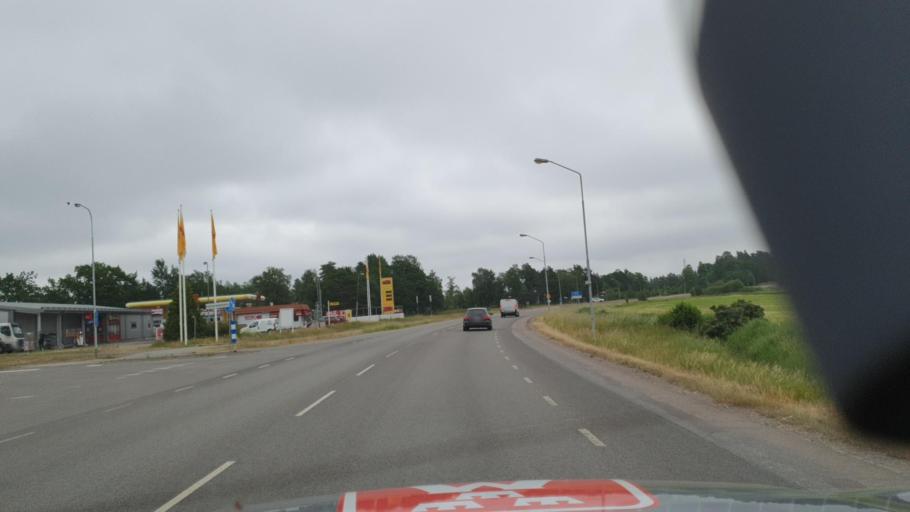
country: SE
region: Kalmar
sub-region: Kalmar Kommun
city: Lindsdal
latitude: 56.7238
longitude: 16.3003
